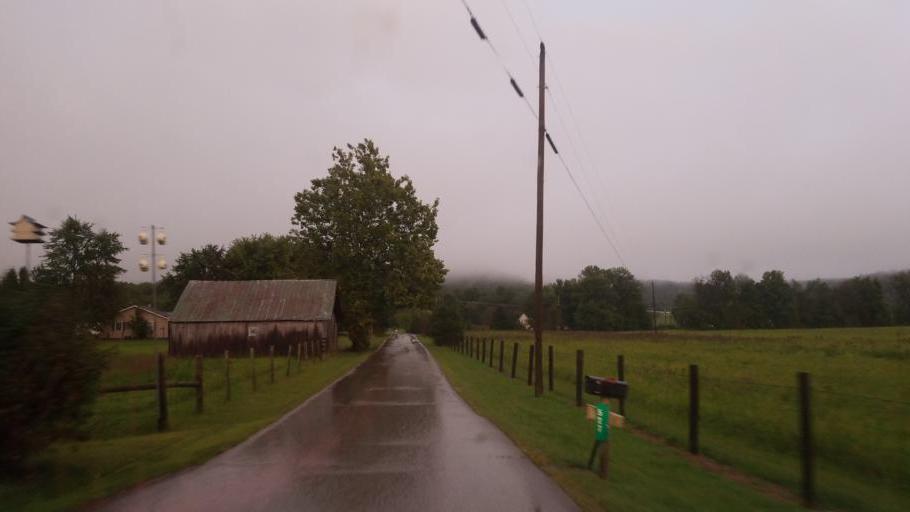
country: US
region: Kentucky
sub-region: Fleming County
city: Flemingsburg
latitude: 38.4495
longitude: -83.6319
